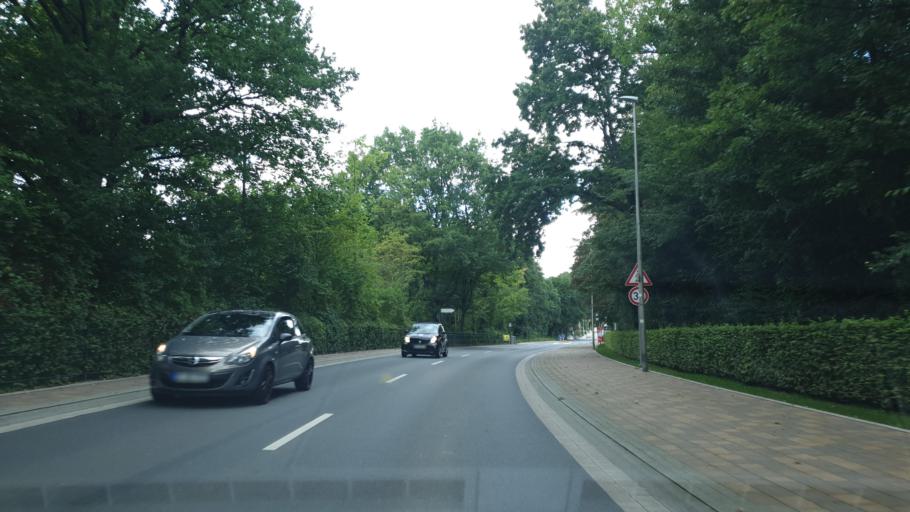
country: DE
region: North Rhine-Westphalia
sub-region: Regierungsbezirk Detmold
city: Hiddenhausen
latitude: 52.1671
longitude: 8.6144
